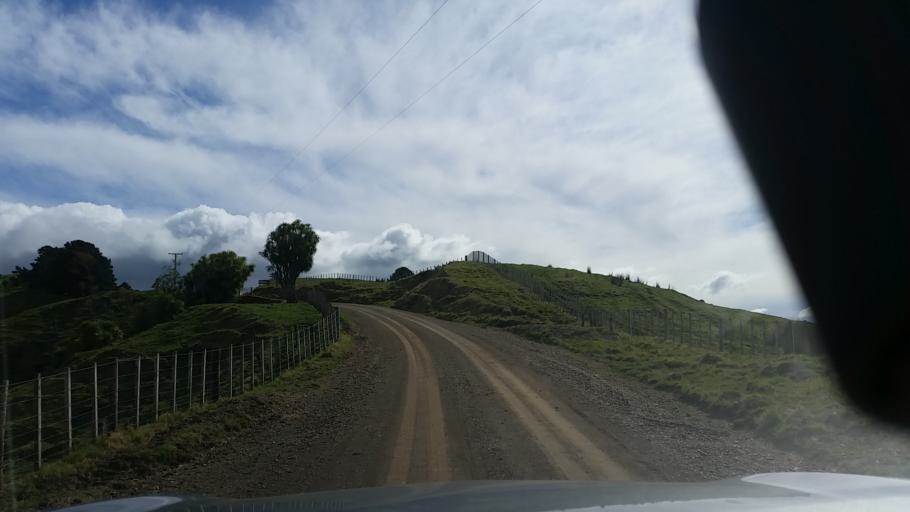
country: NZ
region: Hawke's Bay
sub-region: Napier City
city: Napier
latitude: -39.2152
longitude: 176.9720
